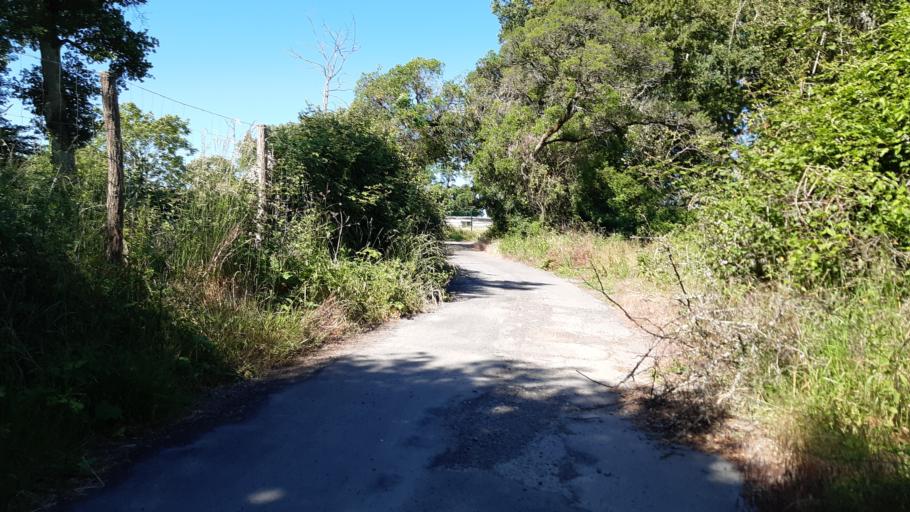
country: FR
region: Centre
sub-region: Departement d'Indre-et-Loire
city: Mettray
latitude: 47.4344
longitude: 0.6590
